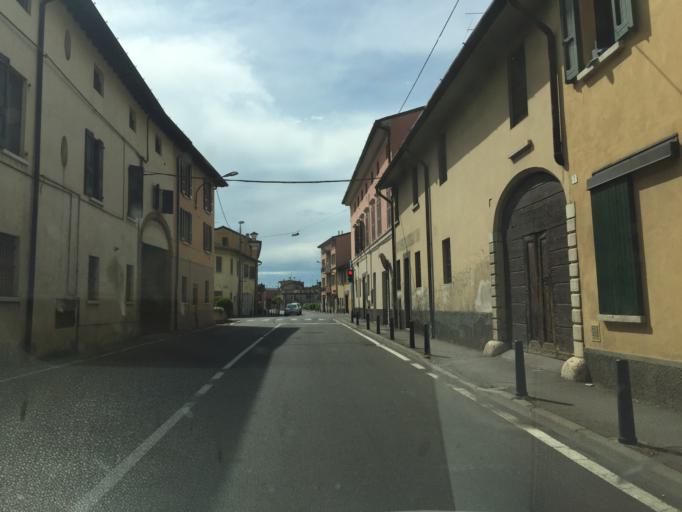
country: IT
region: Lombardy
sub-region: Provincia di Brescia
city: Poncarale
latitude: 45.4590
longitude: 10.1895
